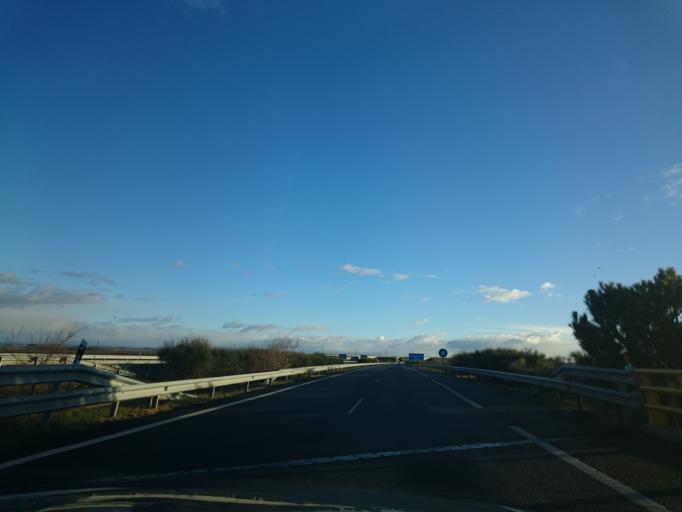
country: ES
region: Castille and Leon
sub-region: Provincia de Leon
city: Villanueva de las Manzanas
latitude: 42.4545
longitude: -5.4873
